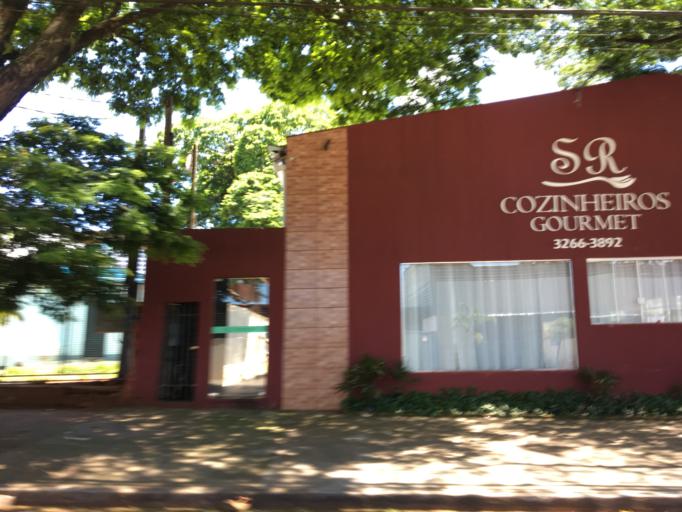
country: BR
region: Parana
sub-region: Maringa
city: Maringa
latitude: -23.4495
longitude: -51.9824
